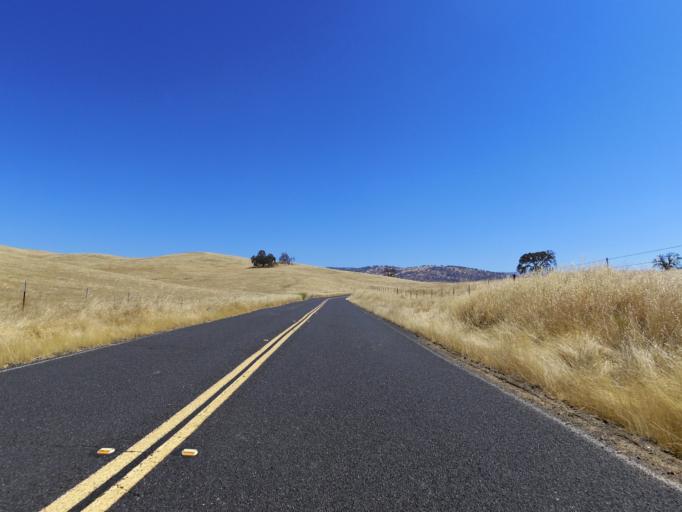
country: US
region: California
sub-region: Mariposa County
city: Mariposa
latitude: 37.4935
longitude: -120.1828
